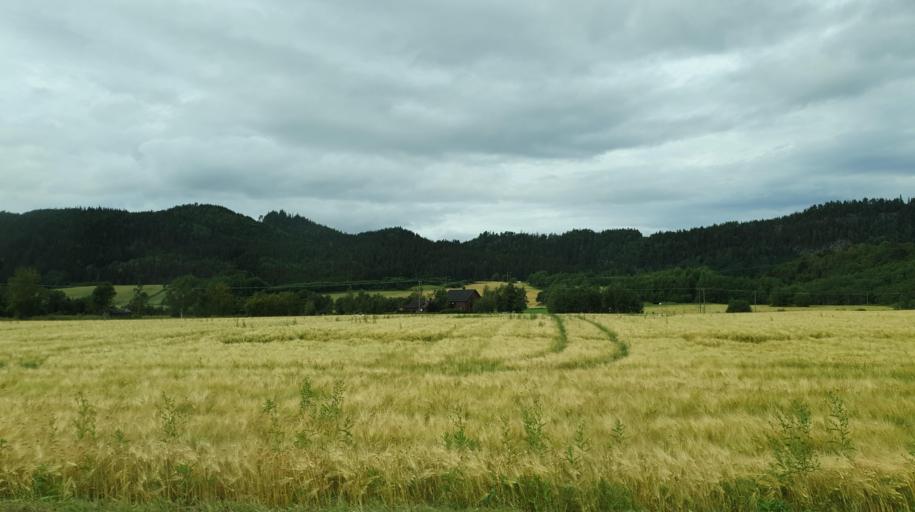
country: NO
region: Nord-Trondelag
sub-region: Stjordal
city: Stjordalshalsen
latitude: 63.4645
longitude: 11.0361
